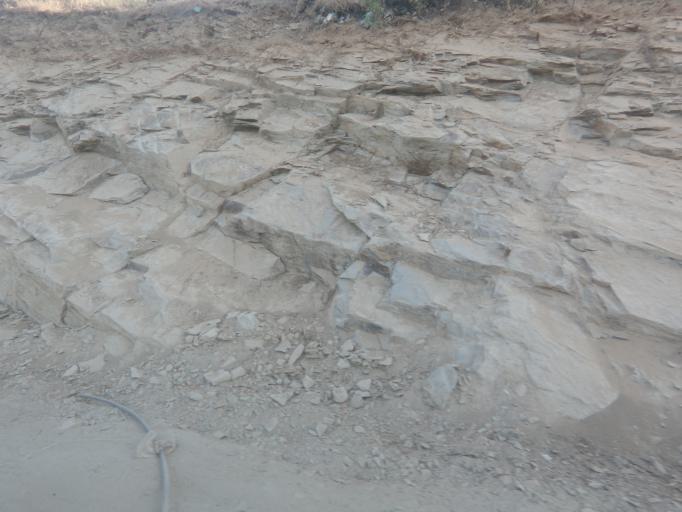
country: PT
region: Viseu
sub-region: Armamar
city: Armamar
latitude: 41.1540
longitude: -7.6436
